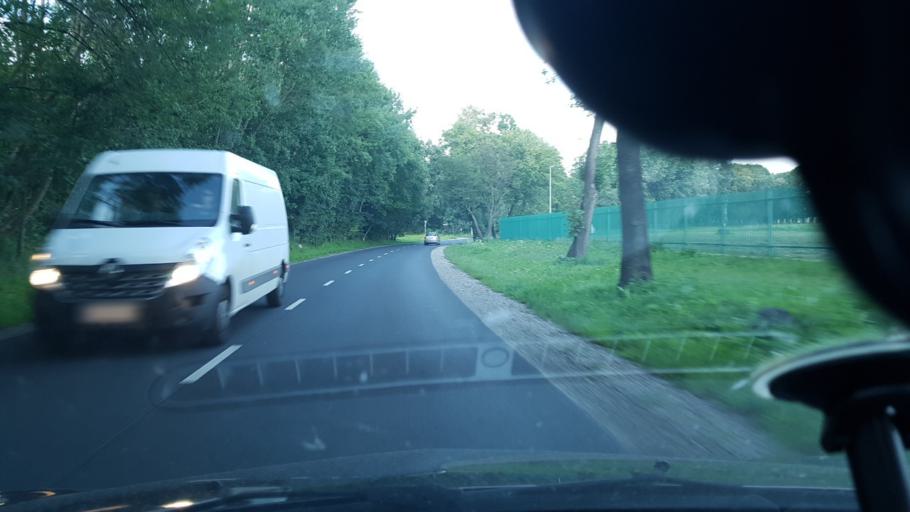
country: PL
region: Lesser Poland Voivodeship
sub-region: Powiat krakowski
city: Kryspinow
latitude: 50.0381
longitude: 19.8284
